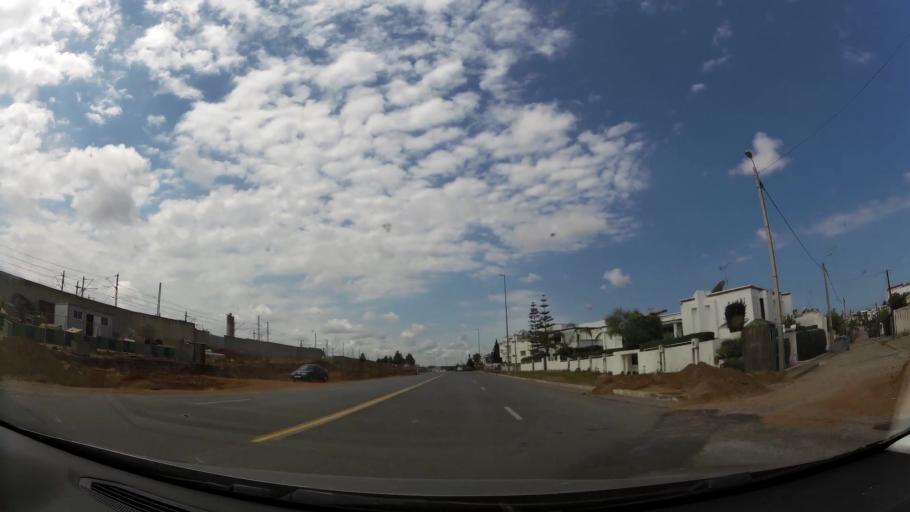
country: MA
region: Gharb-Chrarda-Beni Hssen
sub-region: Kenitra Province
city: Kenitra
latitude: 34.2458
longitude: -6.5963
